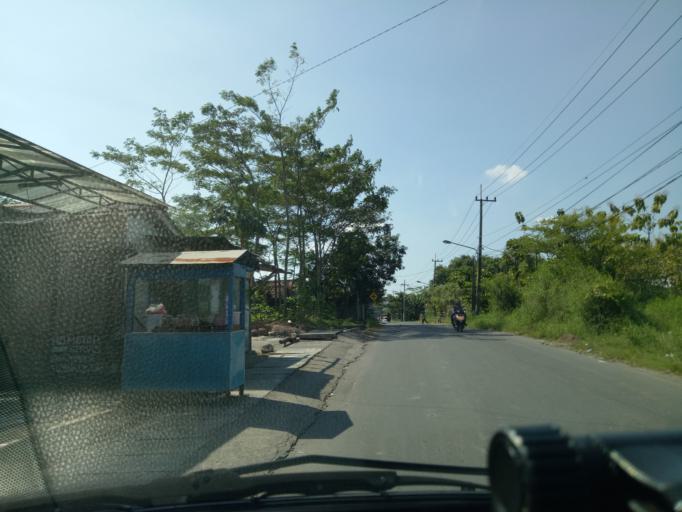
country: ID
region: East Java
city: Driyorejo
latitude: -7.2828
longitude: 112.6359
